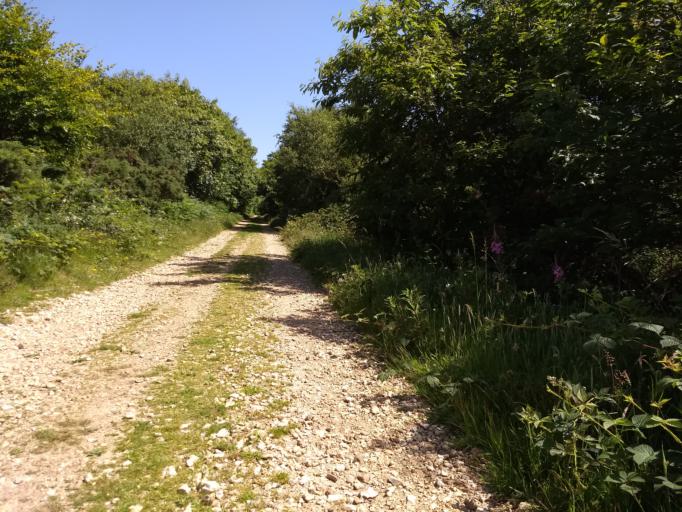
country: GB
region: England
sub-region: Isle of Wight
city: Shalfleet
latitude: 50.6582
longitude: -1.3887
